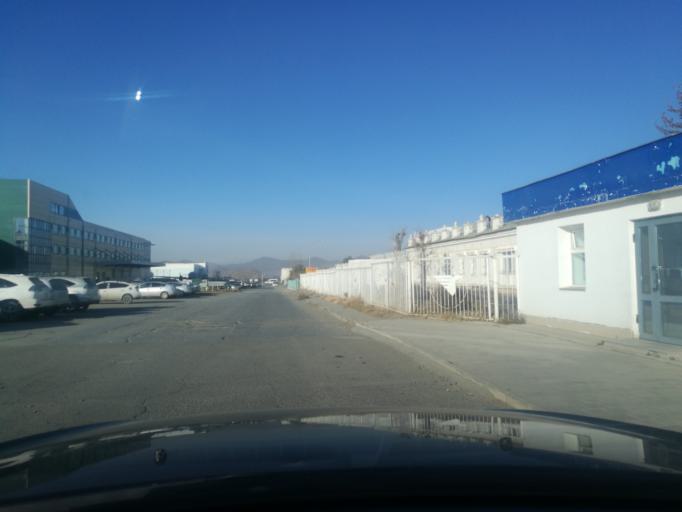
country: MN
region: Ulaanbaatar
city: Ulaanbaatar
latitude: 47.8543
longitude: 106.7604
